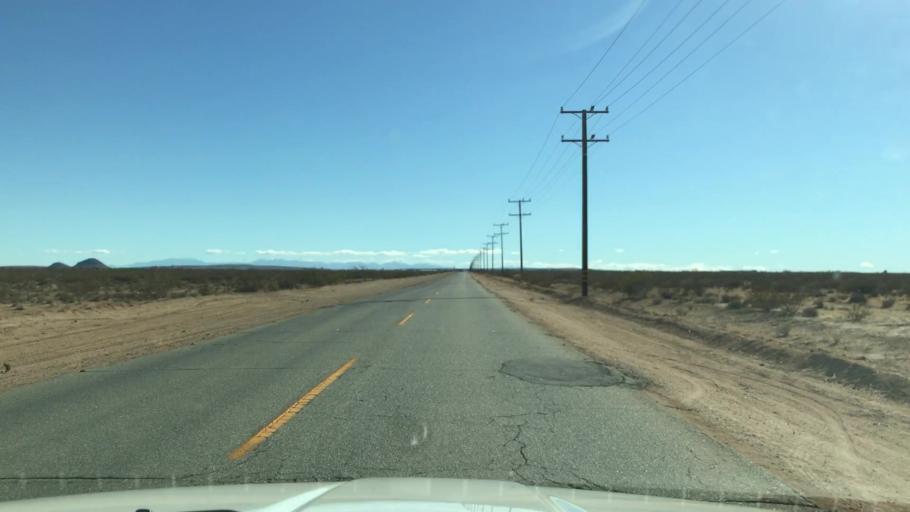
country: US
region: California
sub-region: Kern County
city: California City
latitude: 35.1772
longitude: -117.9858
